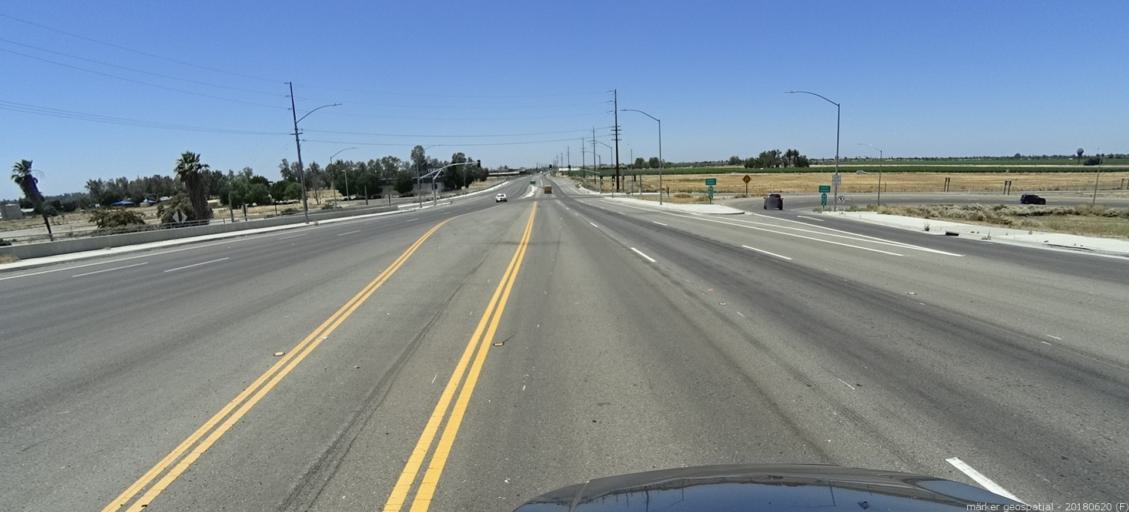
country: US
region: California
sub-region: Madera County
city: Parkwood
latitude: 36.9239
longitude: -120.0232
